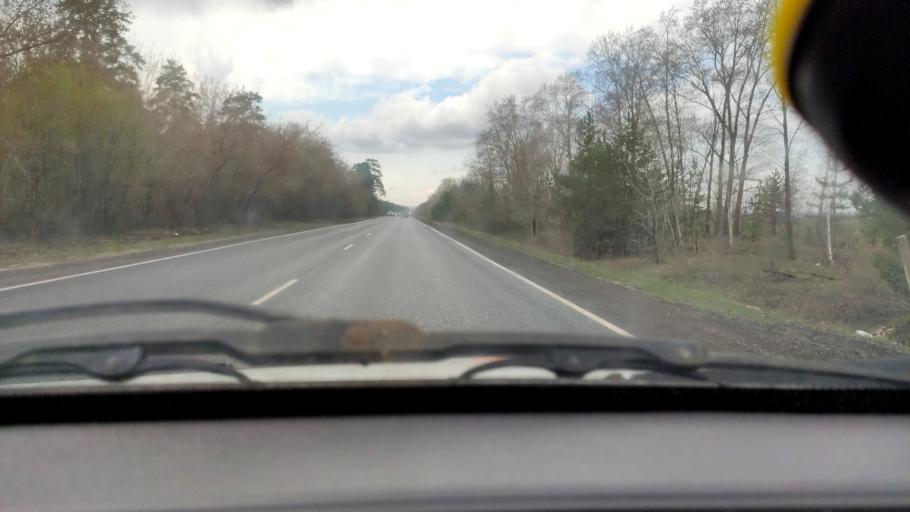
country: RU
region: Samara
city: Povolzhskiy
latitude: 53.6212
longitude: 49.6415
